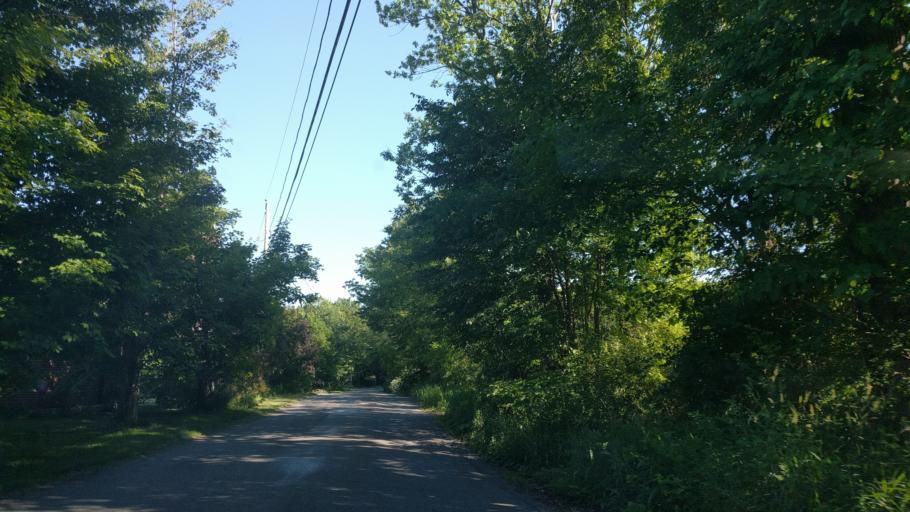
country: US
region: Massachusetts
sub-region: Worcester County
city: Oxford
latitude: 42.1421
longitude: -71.8365
